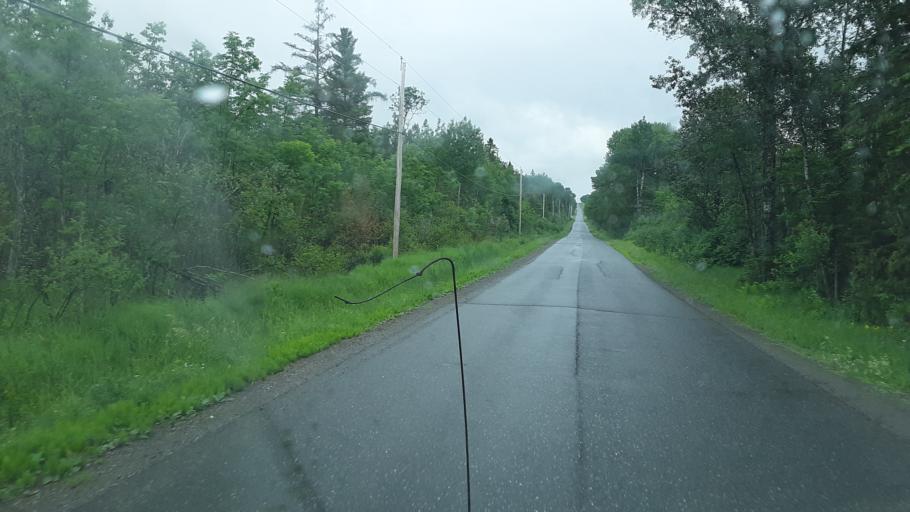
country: US
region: Maine
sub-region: Aroostook County
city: Presque Isle
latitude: 46.6815
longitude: -68.2045
